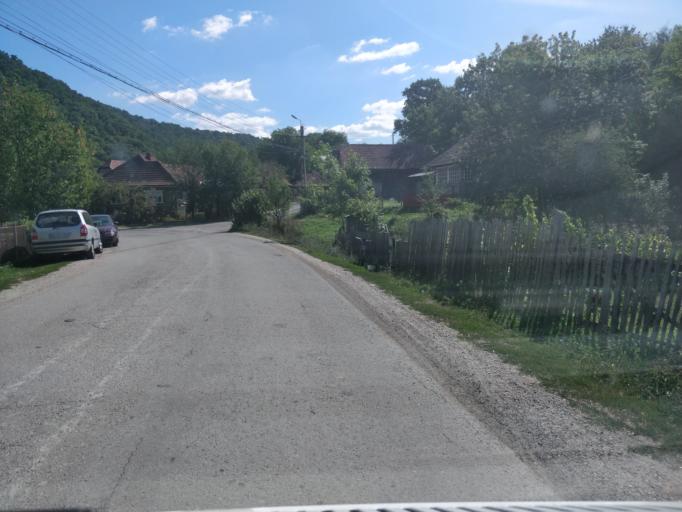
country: RO
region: Cluj
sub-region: Comuna Poeni
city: Poeni
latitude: 46.8921
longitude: 22.8784
